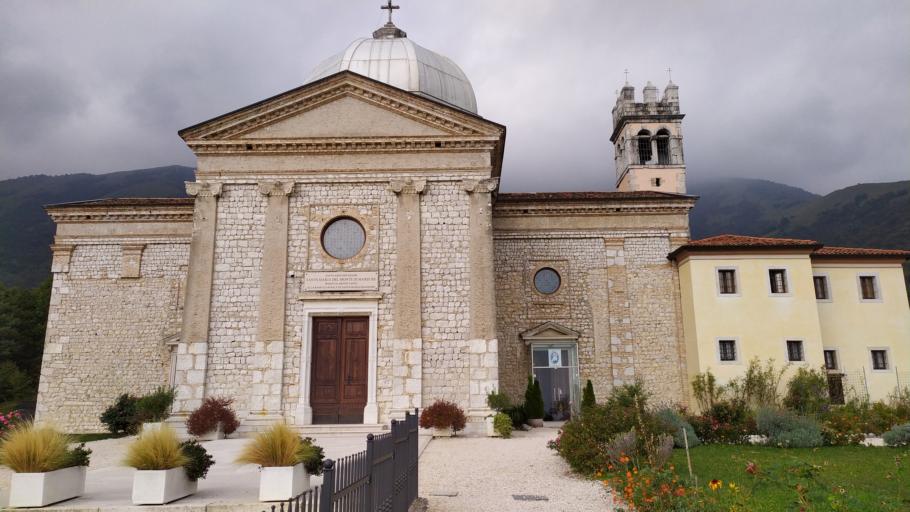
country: IT
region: Friuli Venezia Giulia
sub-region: Provincia di Pordenone
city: Marsure
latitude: 46.0880
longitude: 12.5736
